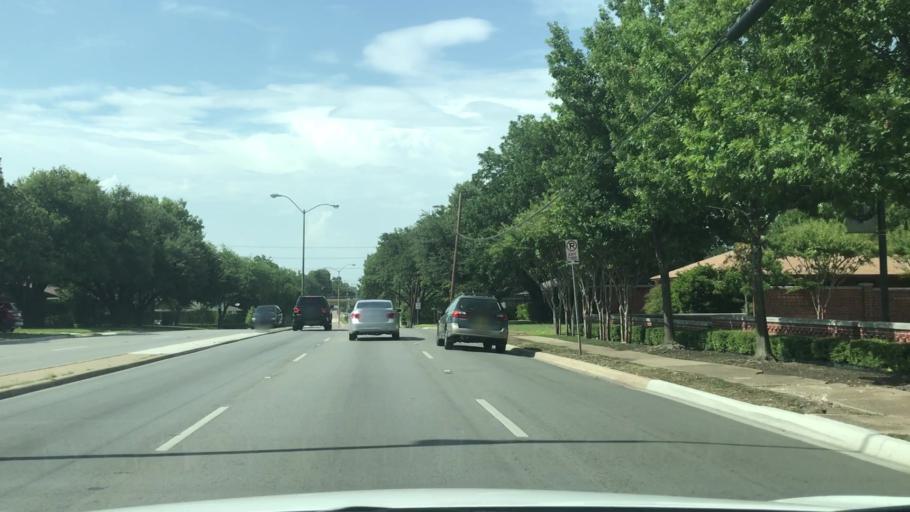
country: US
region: Texas
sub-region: Dallas County
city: Highland Park
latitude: 32.8407
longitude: -96.7529
